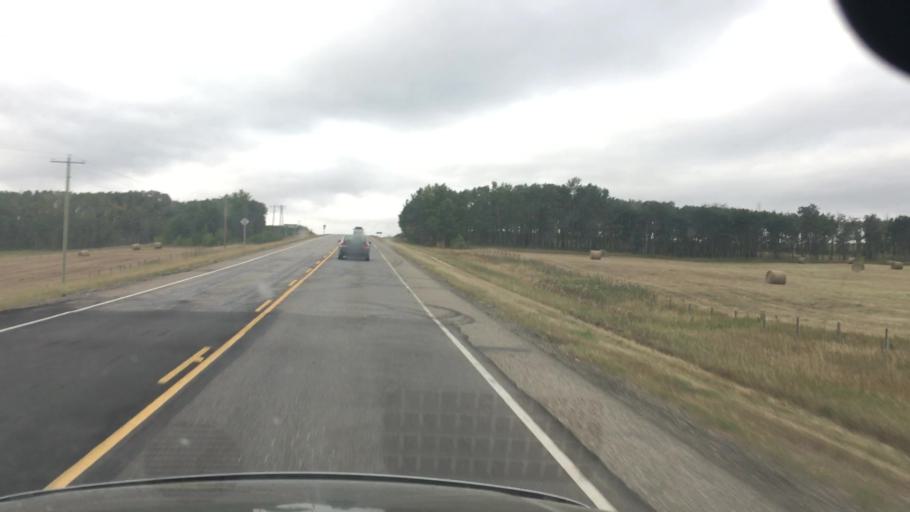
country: CA
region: Alberta
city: Cochrane
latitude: 51.3644
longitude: -114.4726
